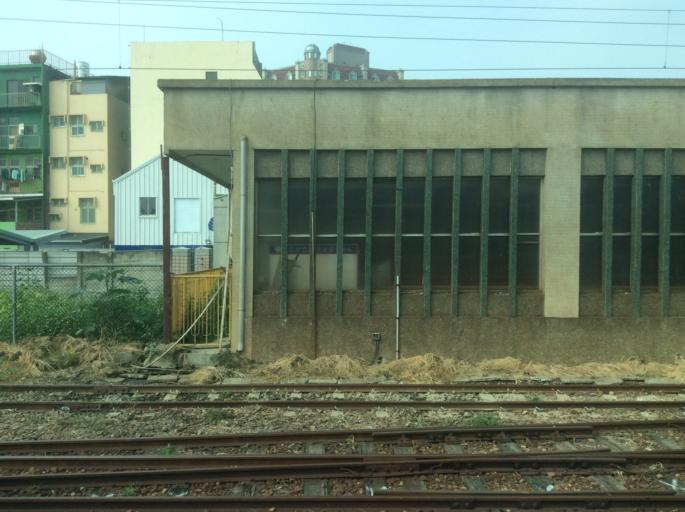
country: TW
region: Taiwan
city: Xinying
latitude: 23.3064
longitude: 120.3230
